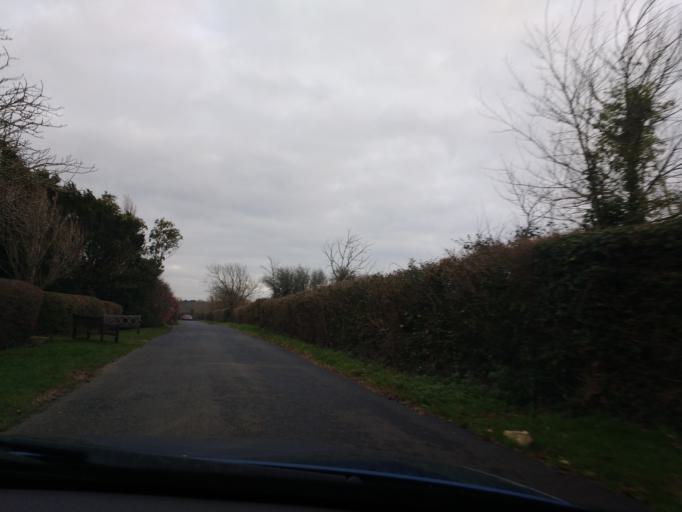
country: GB
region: England
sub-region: Isle of Wight
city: Shalfleet
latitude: 50.7140
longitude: -1.4037
